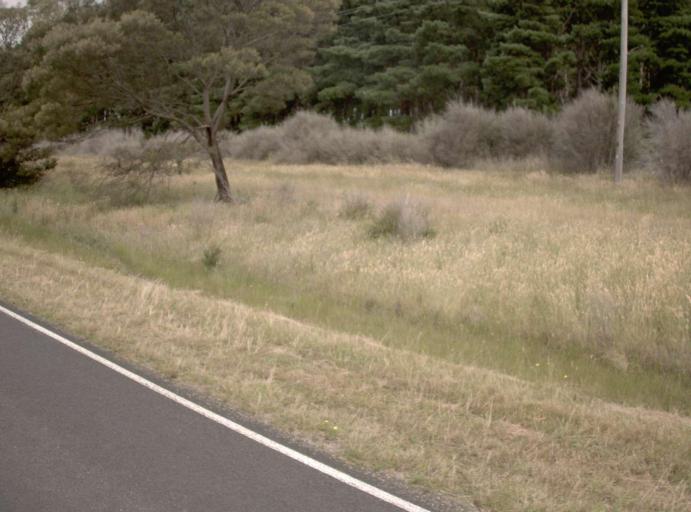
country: AU
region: Victoria
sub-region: Wellington
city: Sale
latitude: -38.1653
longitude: 147.0442
